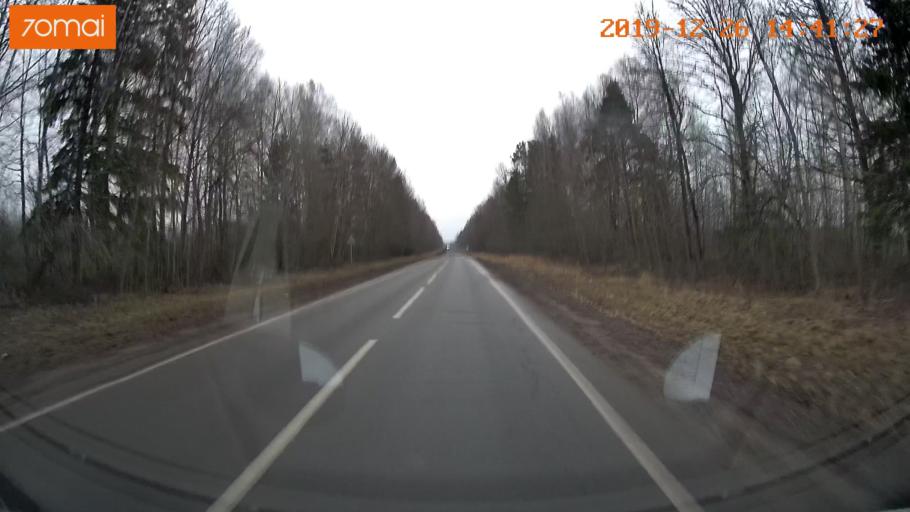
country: RU
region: Jaroslavl
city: Poshekhon'ye
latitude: 58.3714
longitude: 39.0192
